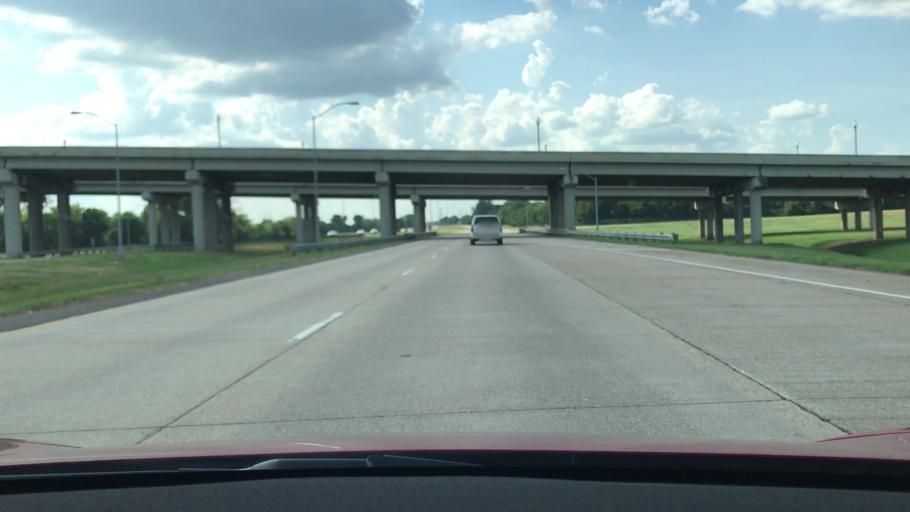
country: US
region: Louisiana
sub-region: Bossier Parish
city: Bossier City
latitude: 32.4938
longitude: -93.6956
